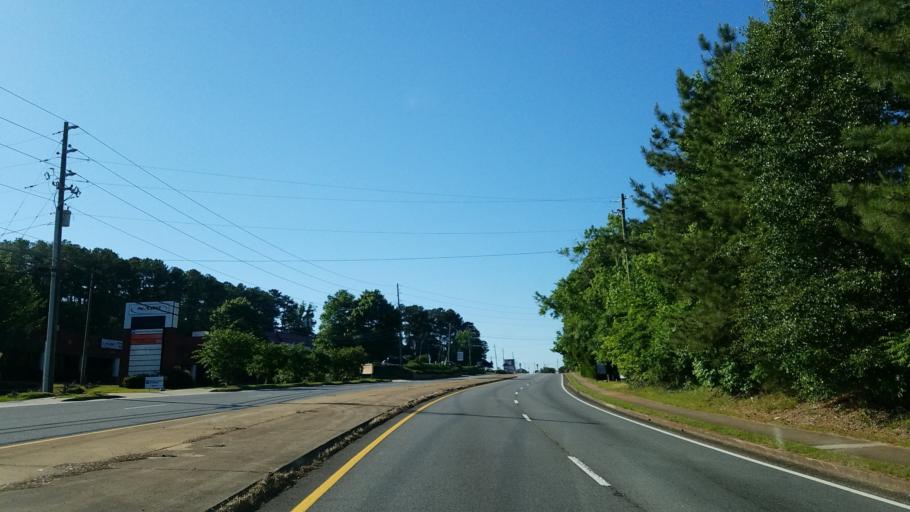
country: US
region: Georgia
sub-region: Cherokee County
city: Woodstock
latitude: 34.0803
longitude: -84.5742
